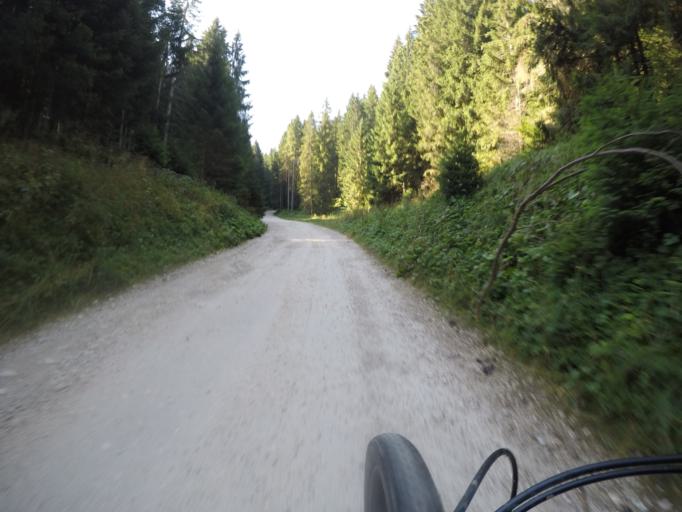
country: IT
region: Veneto
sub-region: Provincia di Vicenza
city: Asiago
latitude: 45.8442
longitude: 11.5242
